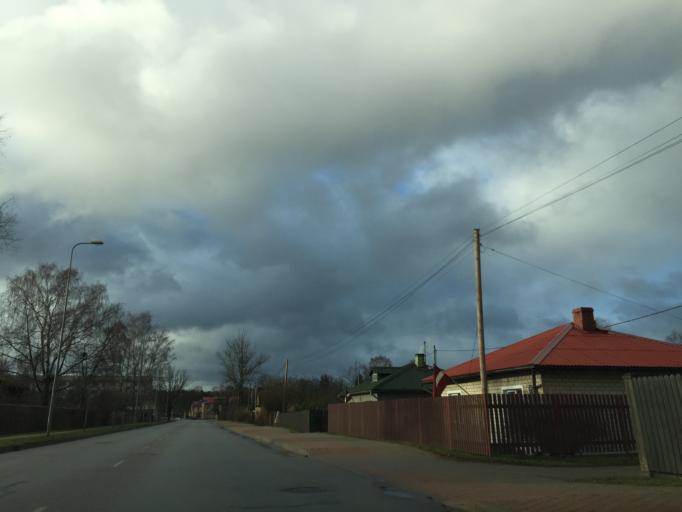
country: LV
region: Valmieras Rajons
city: Valmiera
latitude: 57.5278
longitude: 25.4395
